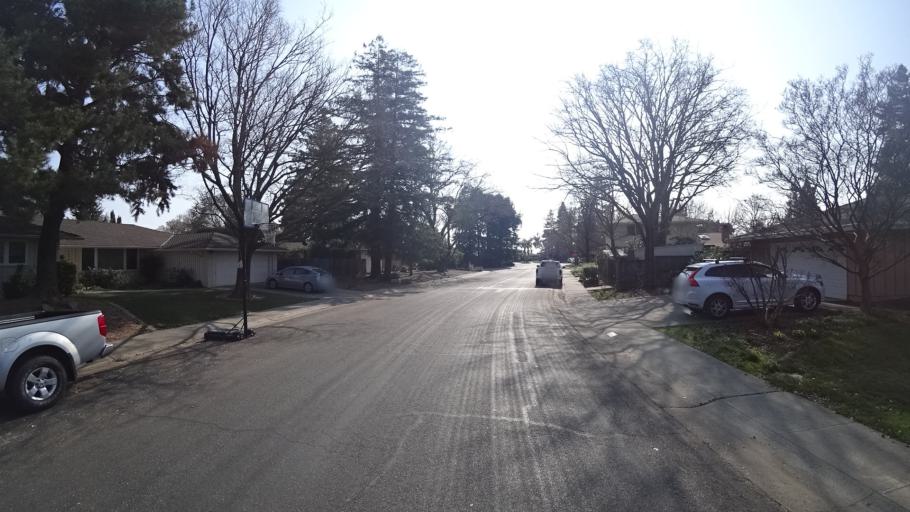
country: US
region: California
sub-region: Yolo County
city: Davis
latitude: 38.5481
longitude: -121.7740
